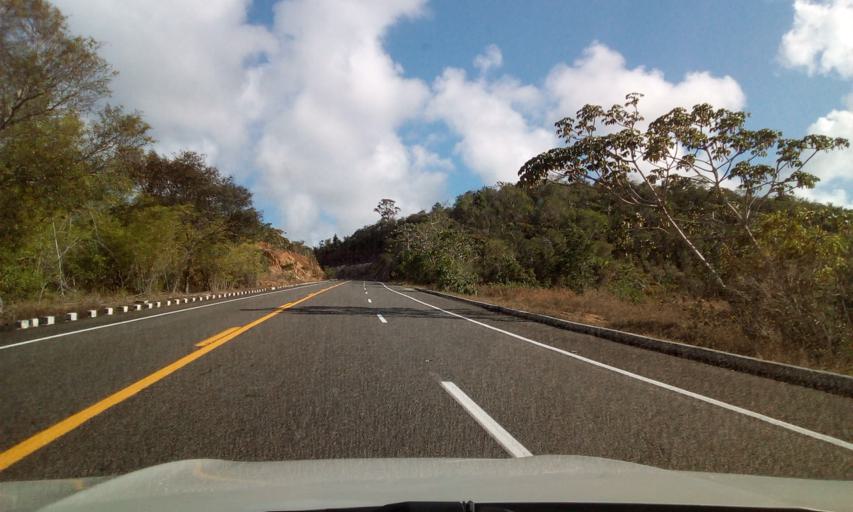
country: BR
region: Bahia
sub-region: Conde
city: Conde
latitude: -11.7675
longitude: -37.5908
